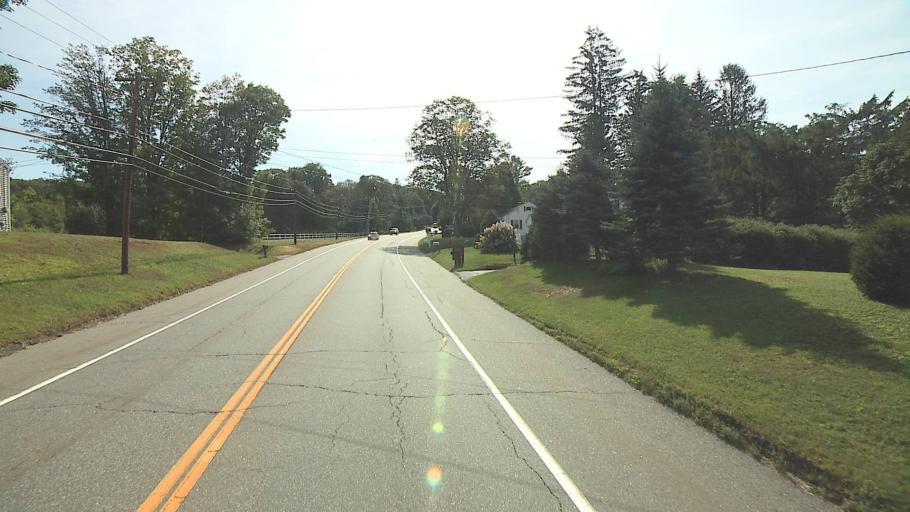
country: US
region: Connecticut
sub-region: Litchfield County
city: Litchfield
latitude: 41.7470
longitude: -73.1784
